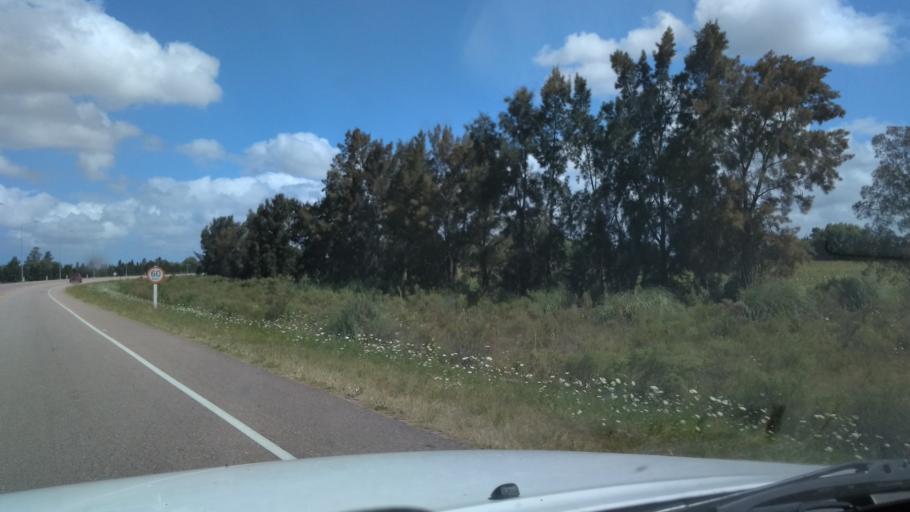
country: UY
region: Canelones
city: Sauce
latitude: -34.6440
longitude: -56.0504
